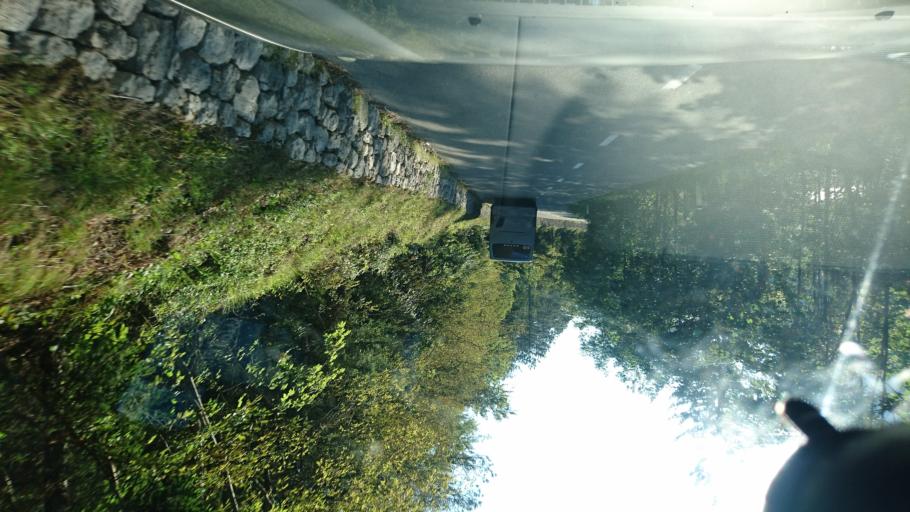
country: SI
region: Bovec
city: Bovec
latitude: 46.3374
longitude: 13.6292
